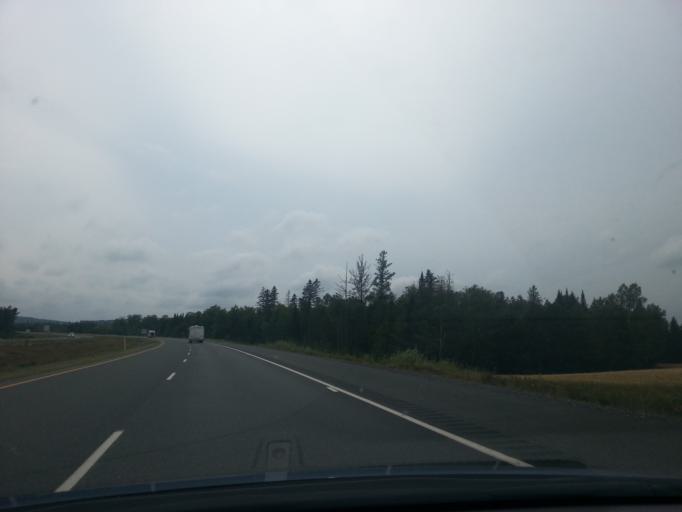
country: CA
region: New Brunswick
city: Florenceville-Bristol
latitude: 46.2697
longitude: -67.5957
